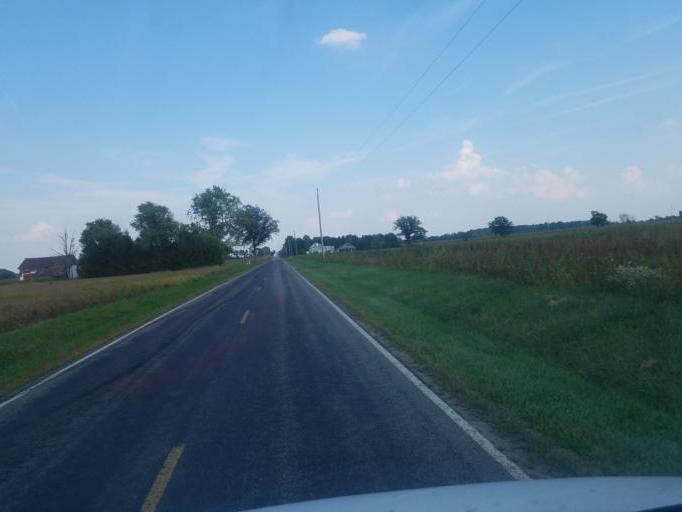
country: US
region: Ohio
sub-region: Hardin County
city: Forest
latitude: 40.9049
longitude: -83.4894
